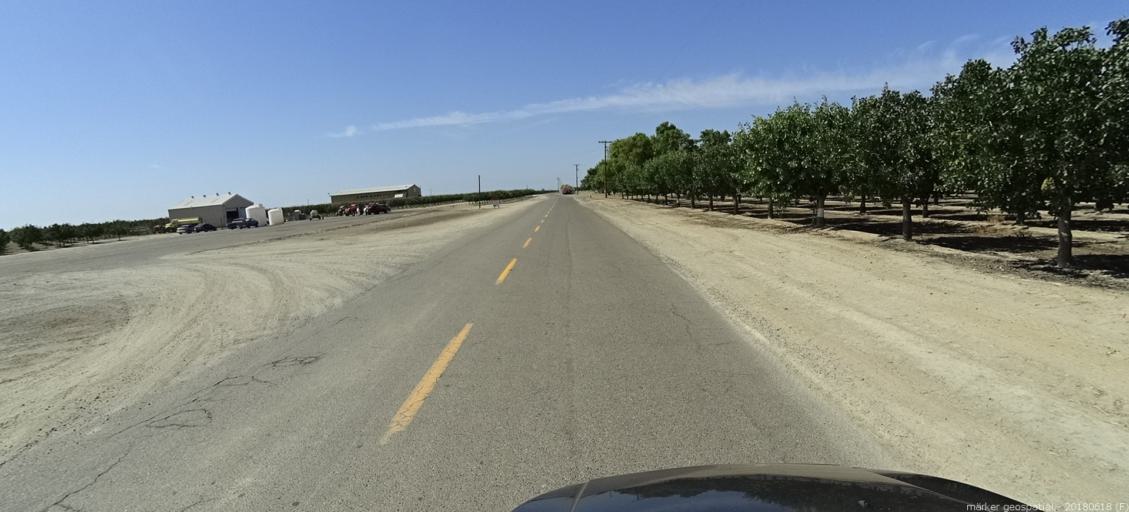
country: US
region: California
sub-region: Fresno County
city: Mendota
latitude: 36.8109
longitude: -120.2592
